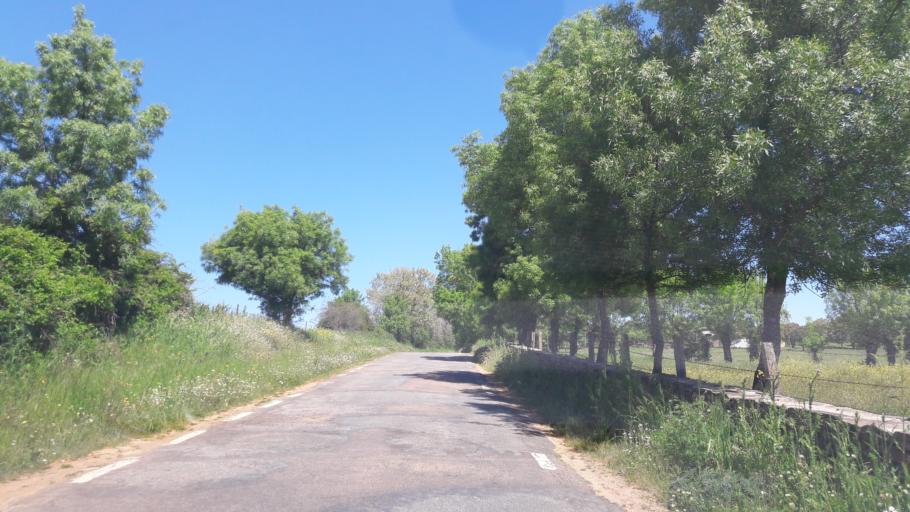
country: ES
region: Castille and Leon
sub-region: Provincia de Salamanca
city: Endrinal
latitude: 40.5751
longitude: -5.8058
